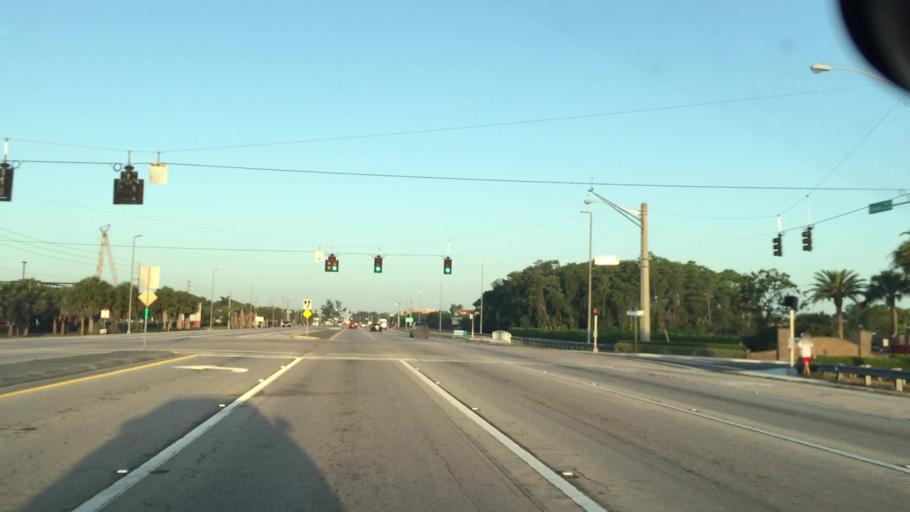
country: US
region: Florida
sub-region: Lee County
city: Villas
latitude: 26.5467
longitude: -81.8427
